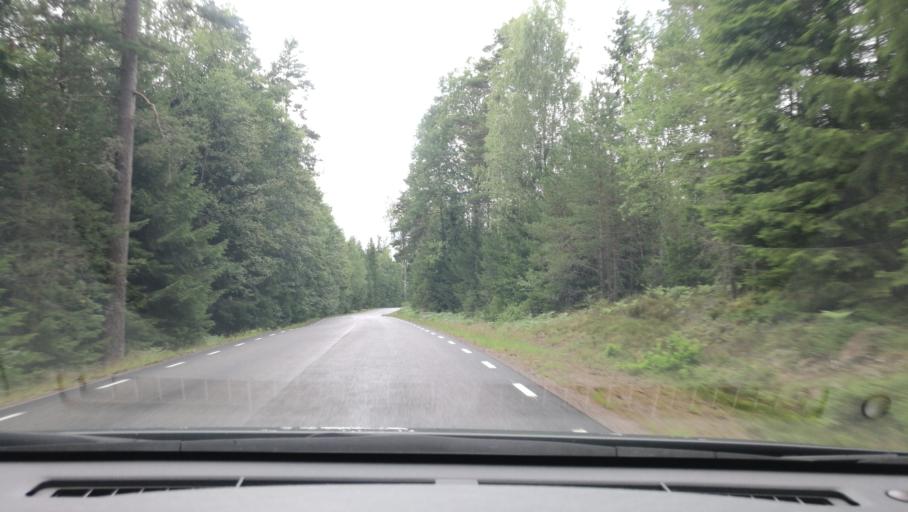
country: SE
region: OEstergoetland
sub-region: Norrkopings Kommun
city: Svartinge
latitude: 58.8166
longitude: 16.0750
